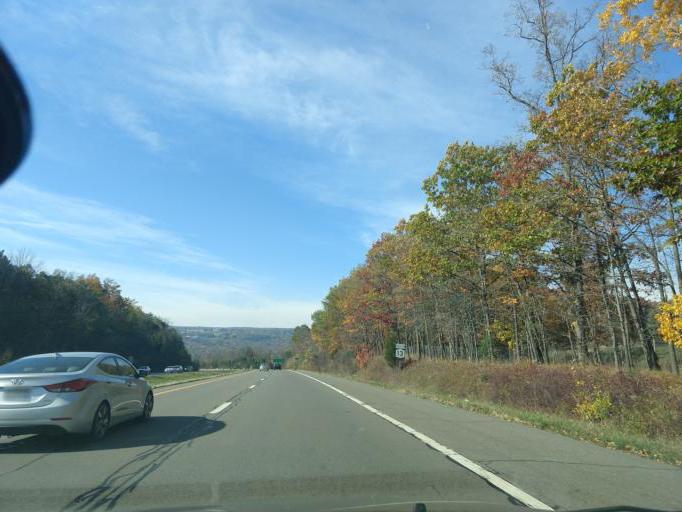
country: US
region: New York
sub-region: Tompkins County
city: Lansing
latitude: 42.4806
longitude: -76.4913
